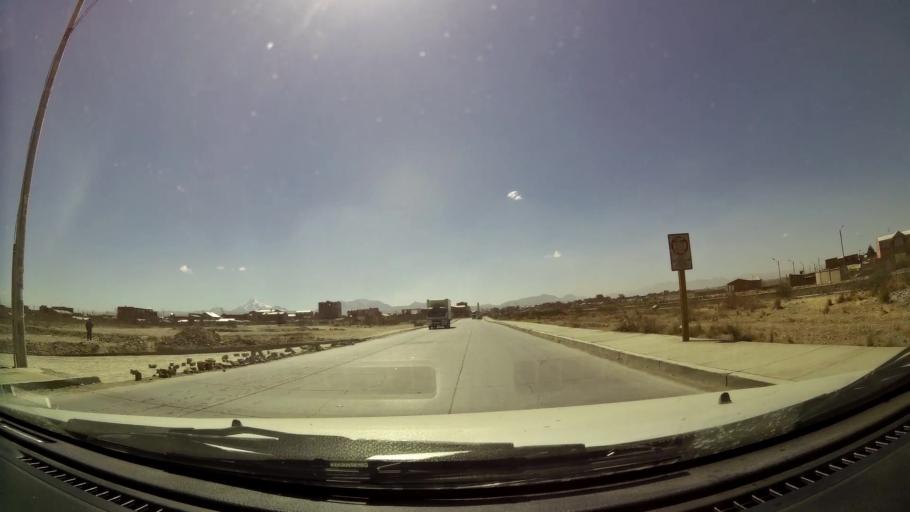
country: BO
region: La Paz
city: La Paz
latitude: -16.5134
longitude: -68.2172
